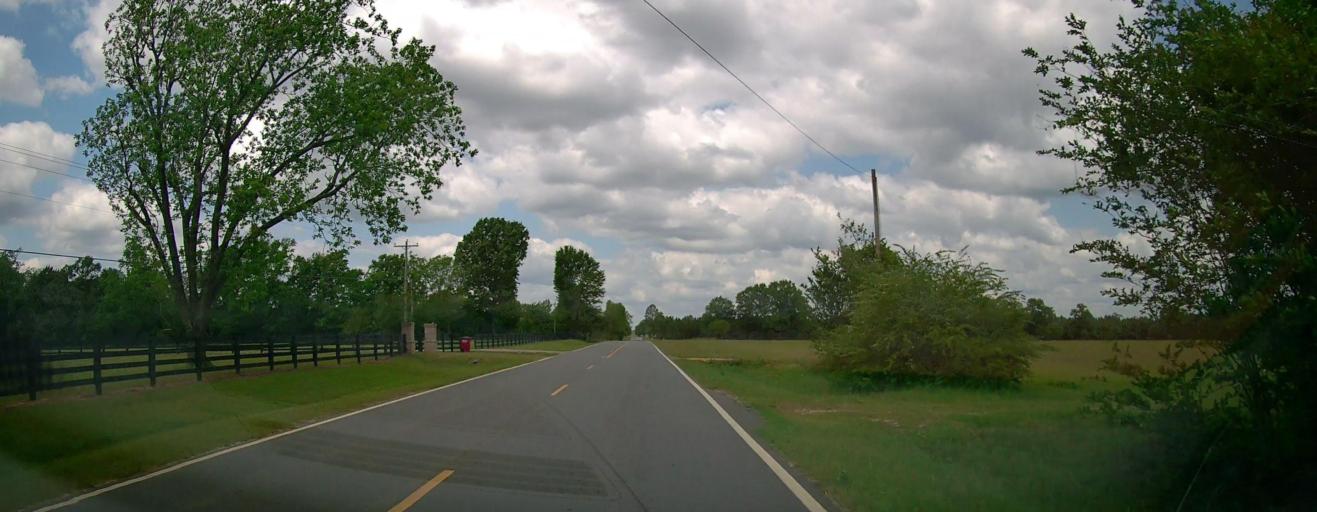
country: US
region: Georgia
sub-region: Laurens County
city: Dublin
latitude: 32.6030
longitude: -82.9589
